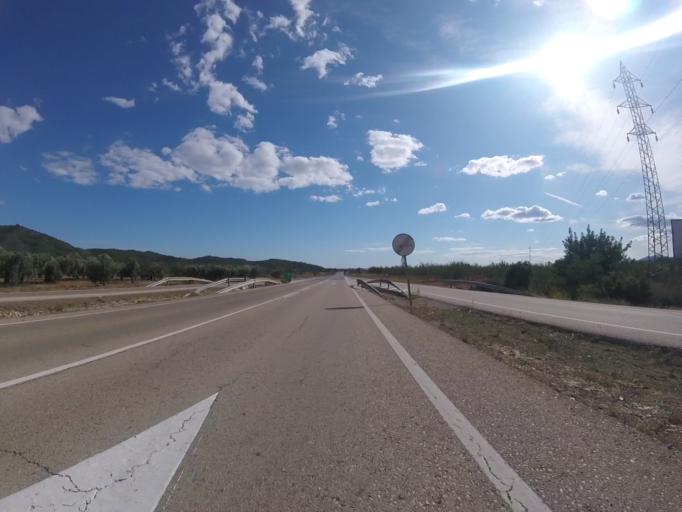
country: ES
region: Valencia
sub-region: Provincia de Castello
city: Alcala de Xivert
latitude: 40.2666
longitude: 0.2416
